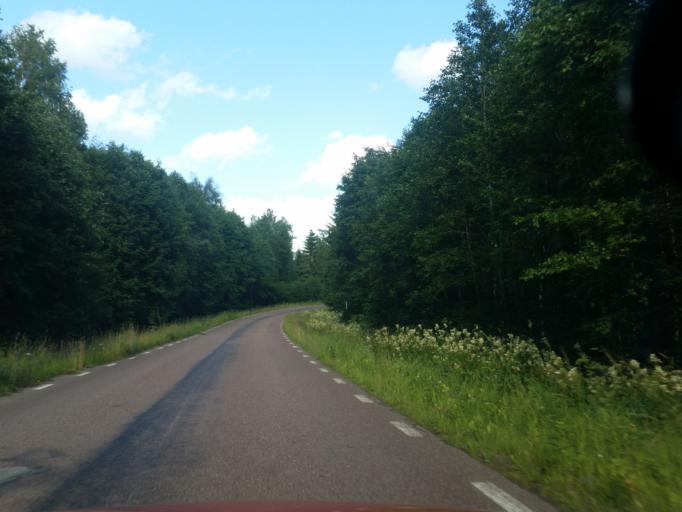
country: SE
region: Dalarna
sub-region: Gagnefs Kommun
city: Gagnef
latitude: 60.6703
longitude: 15.1625
